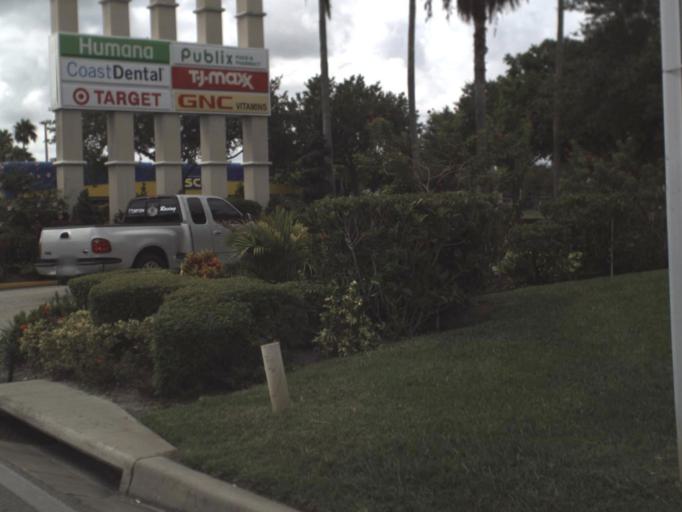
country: US
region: Florida
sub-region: Manatee County
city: Bayshore Gardens
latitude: 27.4331
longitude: -82.5756
